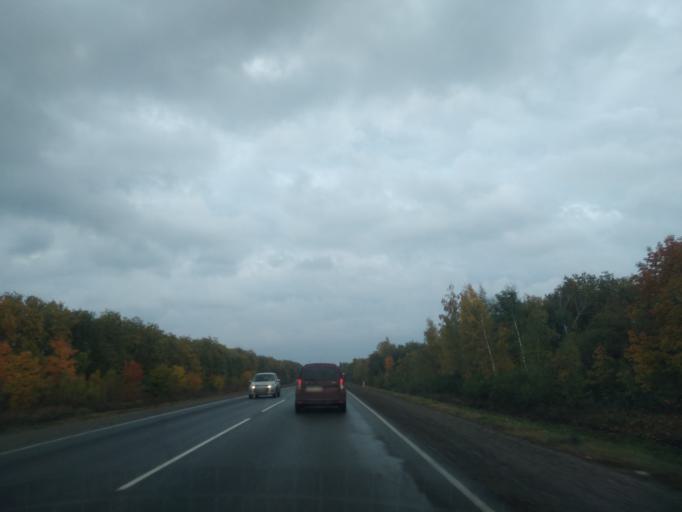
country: RU
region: Lipetsk
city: Syrskoye
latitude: 52.6024
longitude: 39.3735
